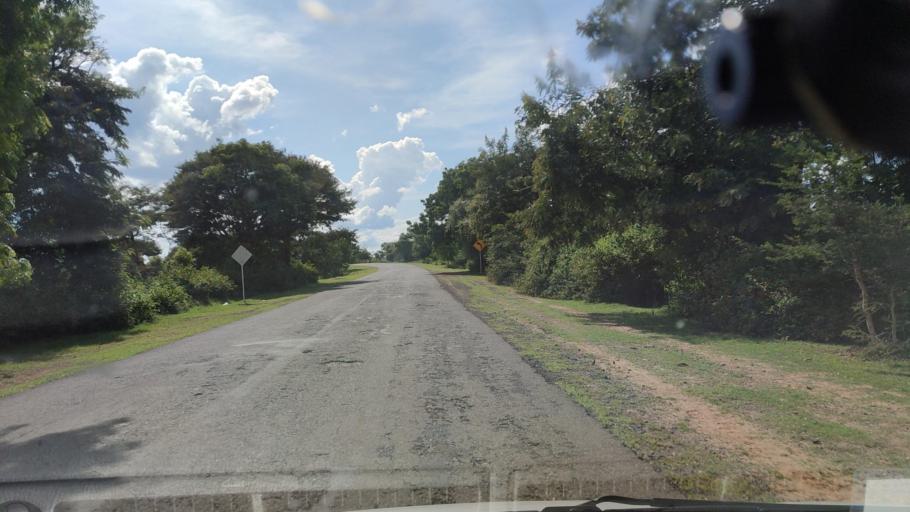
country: MM
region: Mandalay
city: Meiktila
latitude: 20.8116
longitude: 95.5789
